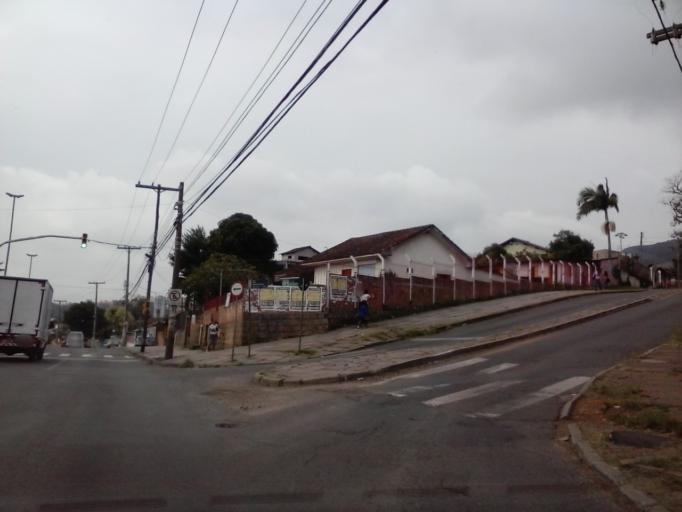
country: BR
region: Rio Grande do Sul
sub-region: Porto Alegre
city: Porto Alegre
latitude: -30.0595
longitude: -51.1484
